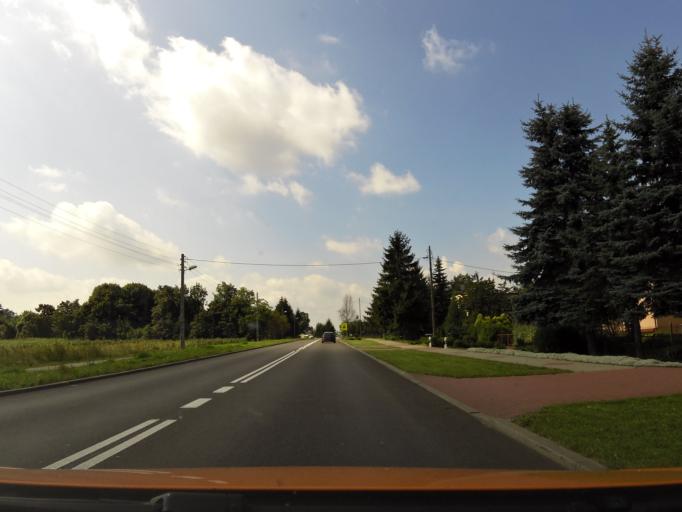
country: PL
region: West Pomeranian Voivodeship
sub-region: Powiat goleniowski
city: Nowogard
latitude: 53.7231
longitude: 15.1926
